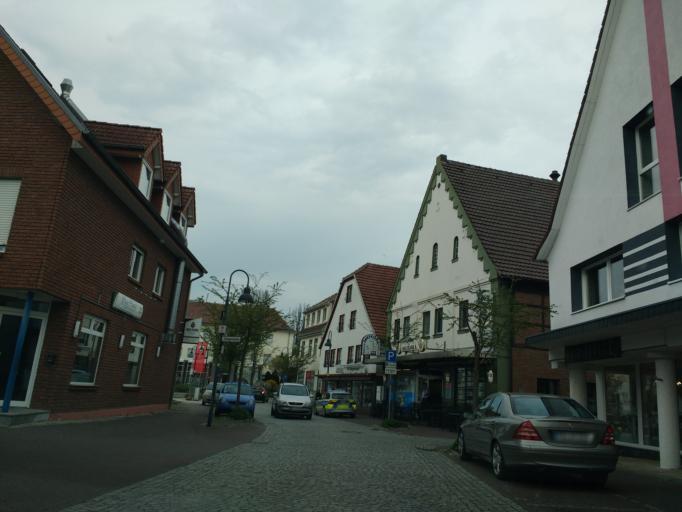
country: DE
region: North Rhine-Westphalia
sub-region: Regierungsbezirk Detmold
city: Salzkotten
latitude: 51.6713
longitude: 8.6050
